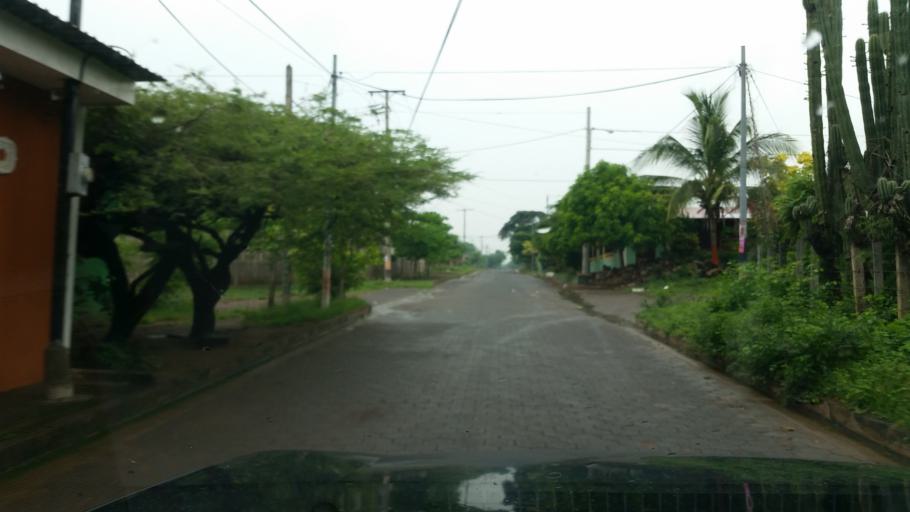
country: NI
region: Granada
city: Granada
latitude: 11.9341
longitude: -85.9646
